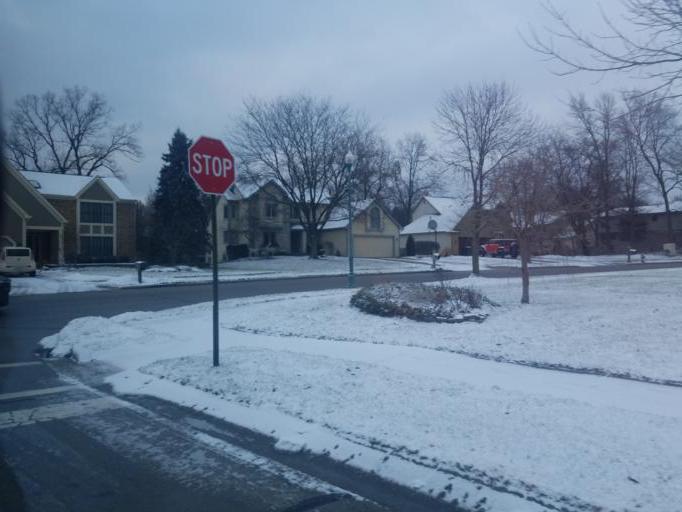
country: US
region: Ohio
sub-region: Franklin County
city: Gahanna
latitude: 40.0443
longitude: -82.8543
